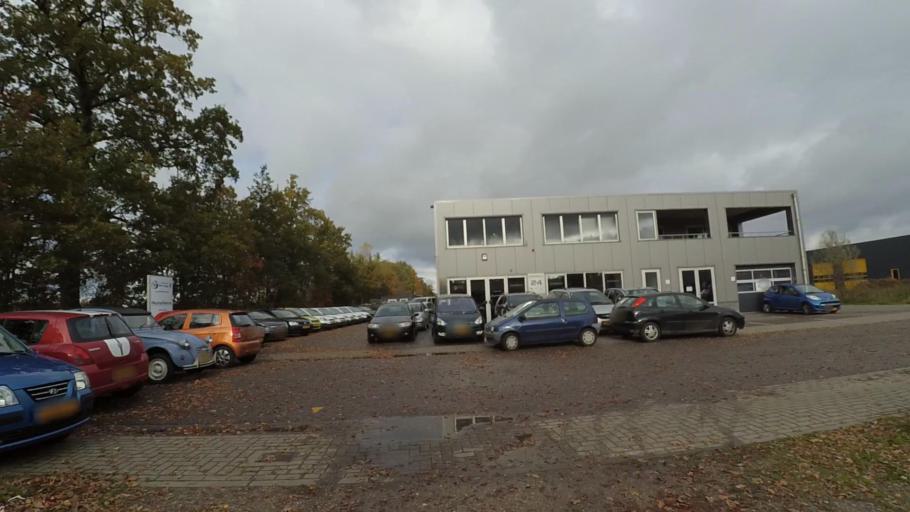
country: NL
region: Gelderland
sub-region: Gemeente Barneveld
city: Terschuur
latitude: 52.1368
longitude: 5.5050
